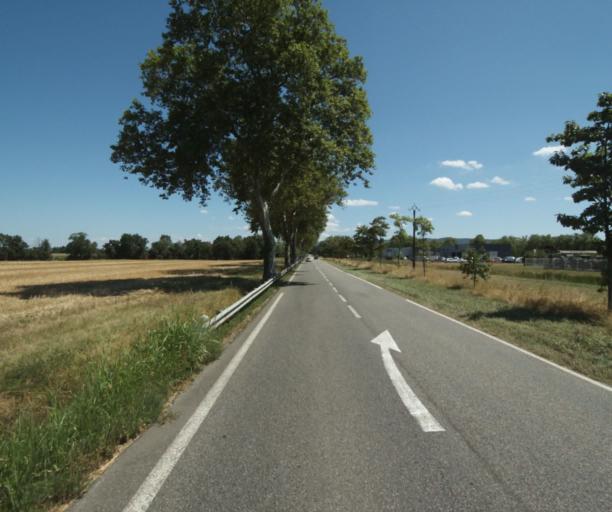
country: FR
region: Midi-Pyrenees
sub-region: Departement de la Haute-Garonne
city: Saint-Felix-Lauragais
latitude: 43.4464
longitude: 1.9419
